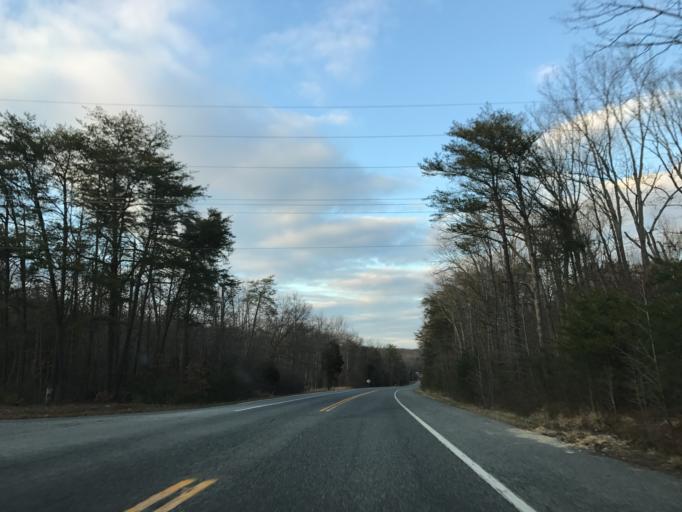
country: US
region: Maryland
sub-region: Cecil County
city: Charlestown
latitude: 39.5298
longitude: -75.9536
